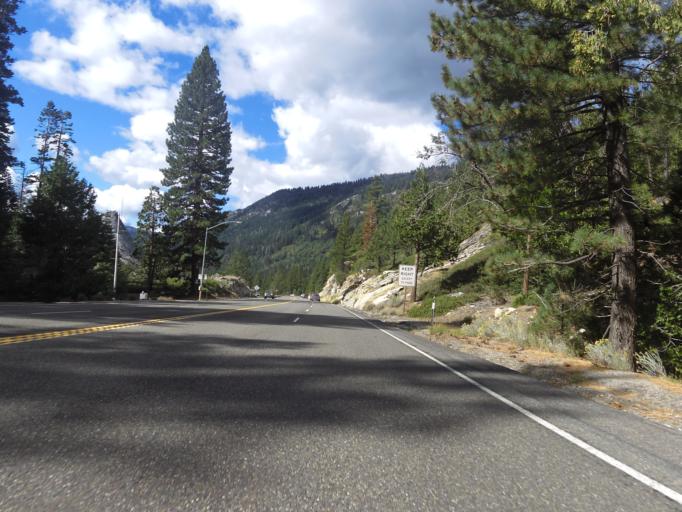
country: US
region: California
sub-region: El Dorado County
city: South Lake Tahoe
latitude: 38.8108
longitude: -120.1261
